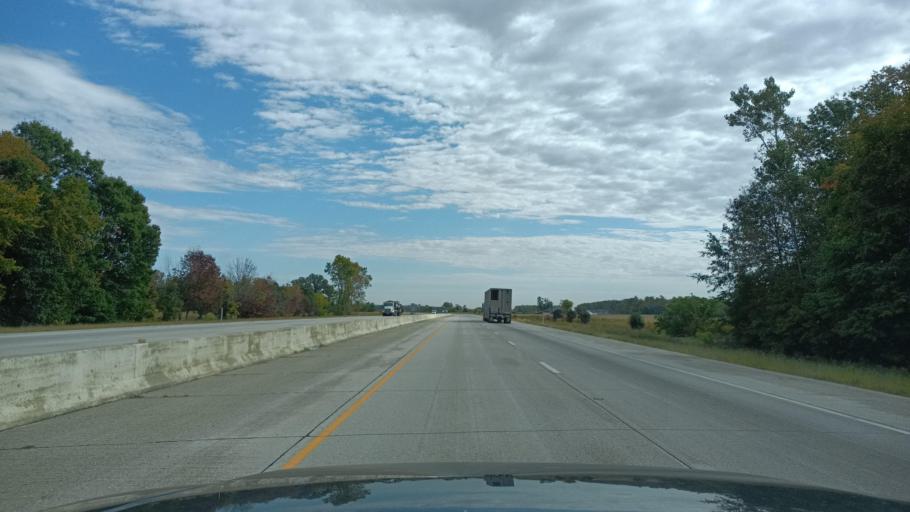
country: US
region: Indiana
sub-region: Wells County
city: Ossian
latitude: 40.9558
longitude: -85.1481
